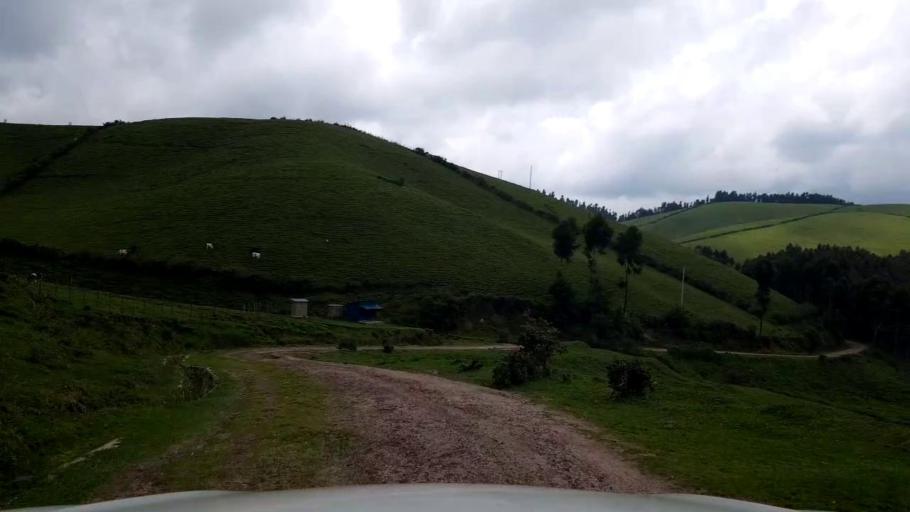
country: RW
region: Western Province
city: Gisenyi
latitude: -1.6824
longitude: 29.4173
